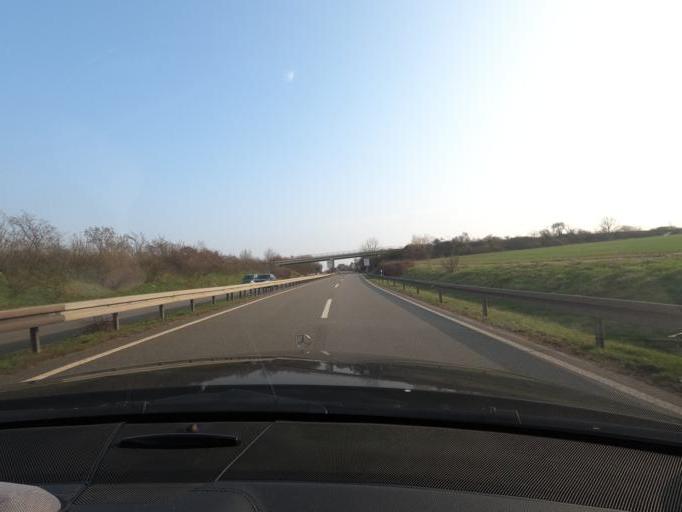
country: DE
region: Thuringia
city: Elxleben
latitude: 51.0183
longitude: 10.9826
